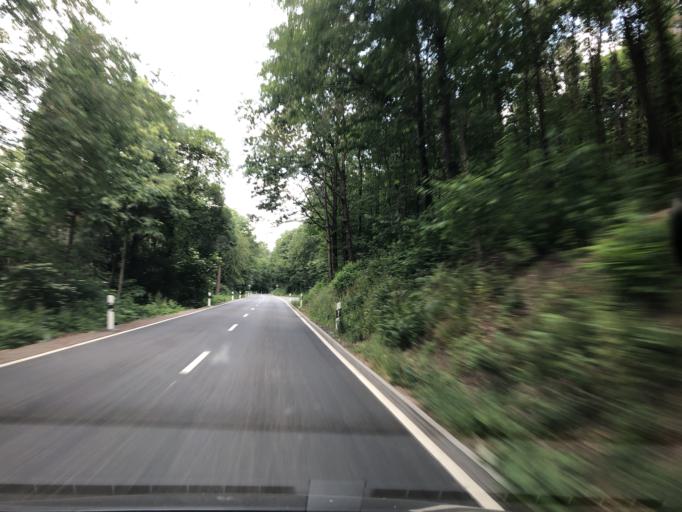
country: DE
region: Baden-Wuerttemberg
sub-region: Karlsruhe Region
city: Heidelberg
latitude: 49.3937
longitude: 8.7143
